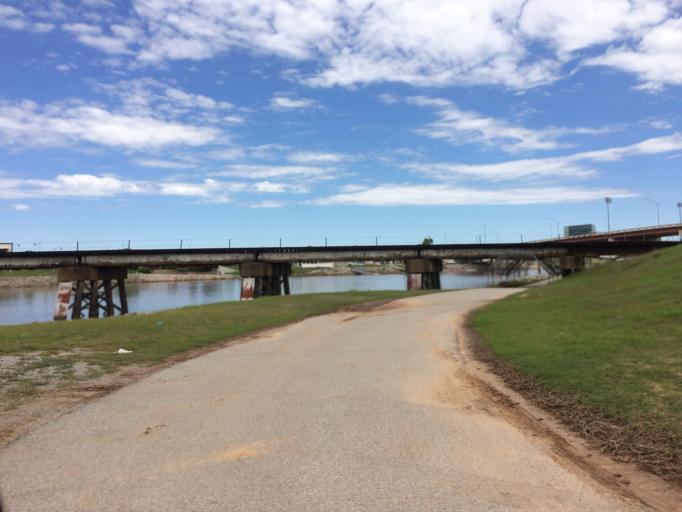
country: US
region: Oklahoma
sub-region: Oklahoma County
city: Oklahoma City
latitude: 35.4551
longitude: -97.5052
